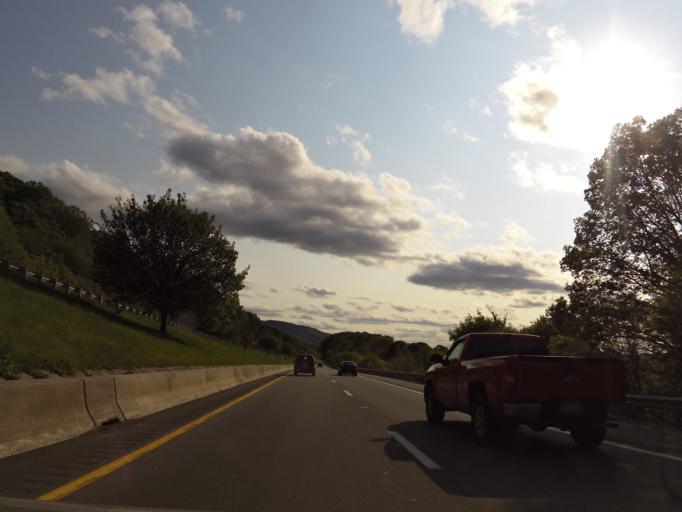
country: US
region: West Virginia
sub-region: Mercer County
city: Bluefield
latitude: 37.2523
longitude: -81.2027
